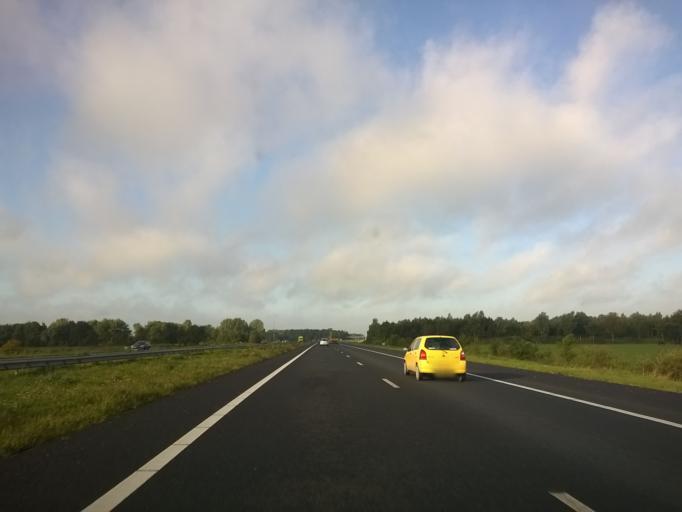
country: NL
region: Groningen
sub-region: Gemeente Zuidhorn
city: Zuidhorn
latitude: 53.1958
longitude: 6.4381
